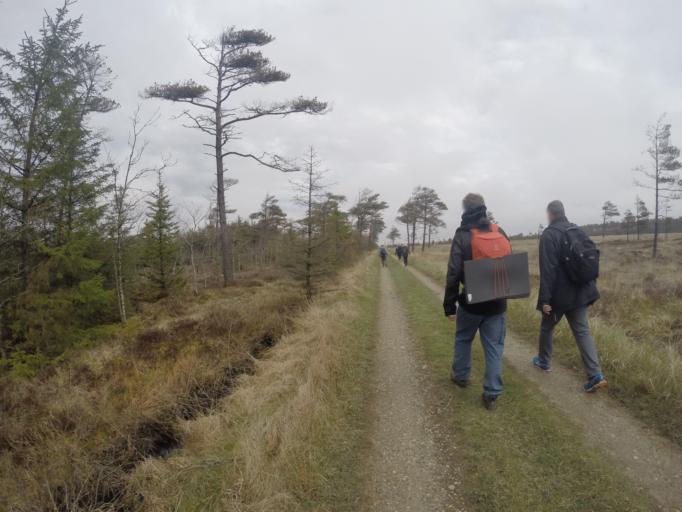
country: DK
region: North Denmark
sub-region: Thisted Kommune
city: Hanstholm
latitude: 57.0414
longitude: 8.5588
